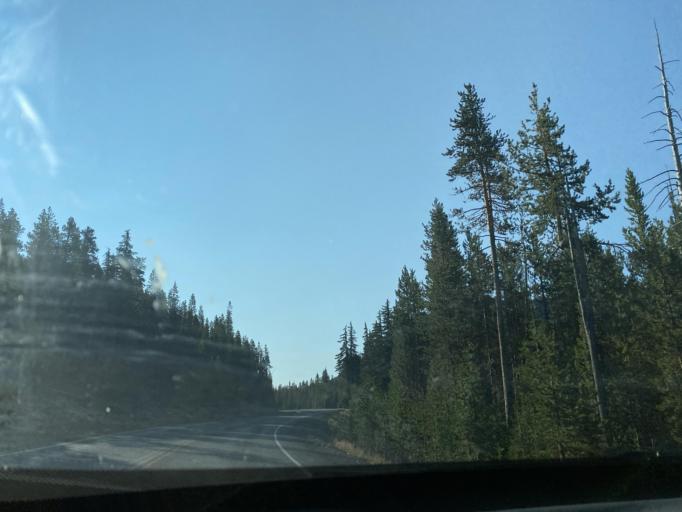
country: US
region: Oregon
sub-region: Deschutes County
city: Three Rivers
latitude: 43.7067
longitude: -121.2665
